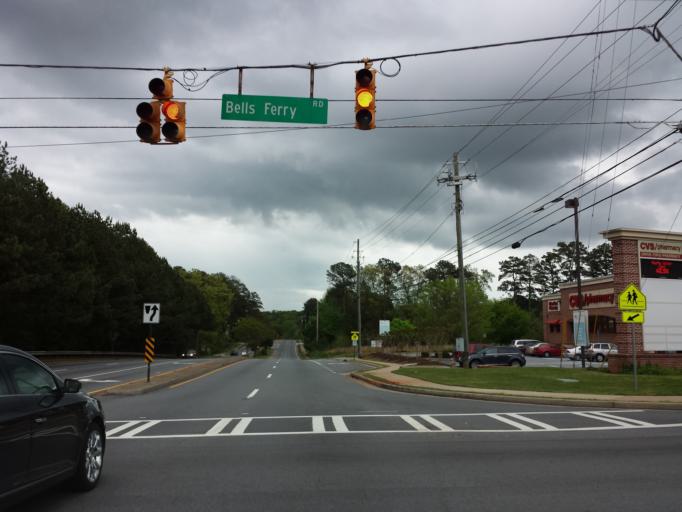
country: US
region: Georgia
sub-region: Cobb County
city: Marietta
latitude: 34.0138
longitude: -84.5484
